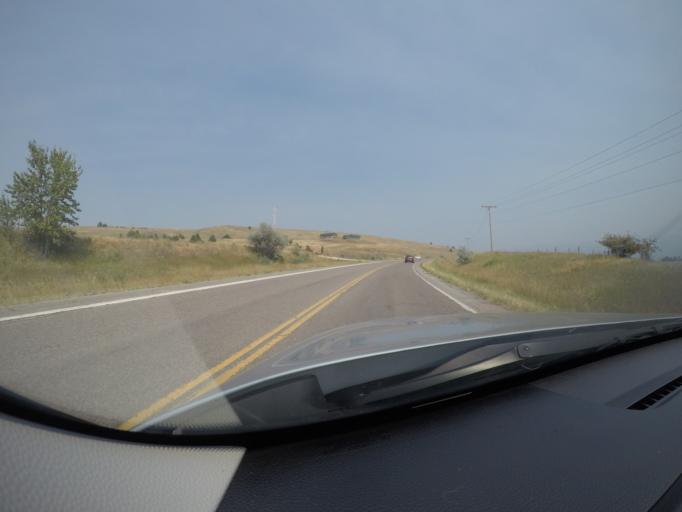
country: US
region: Montana
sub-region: Lake County
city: Polson
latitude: 47.7340
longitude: -114.1882
